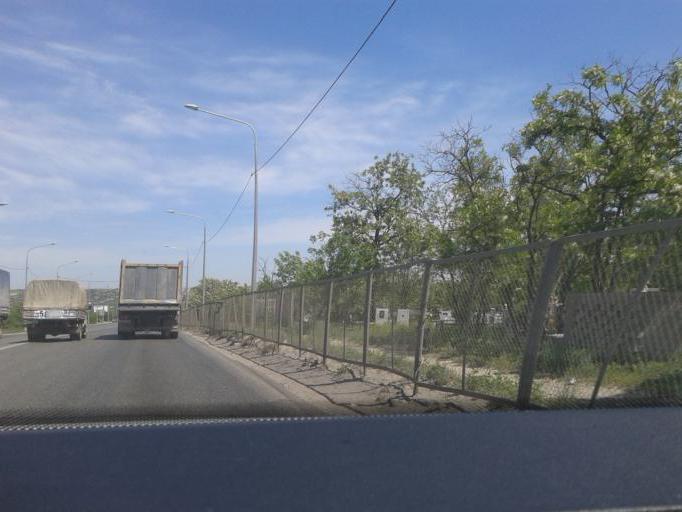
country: RU
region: Volgograd
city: Gorodishche
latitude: 48.7855
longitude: 44.5204
